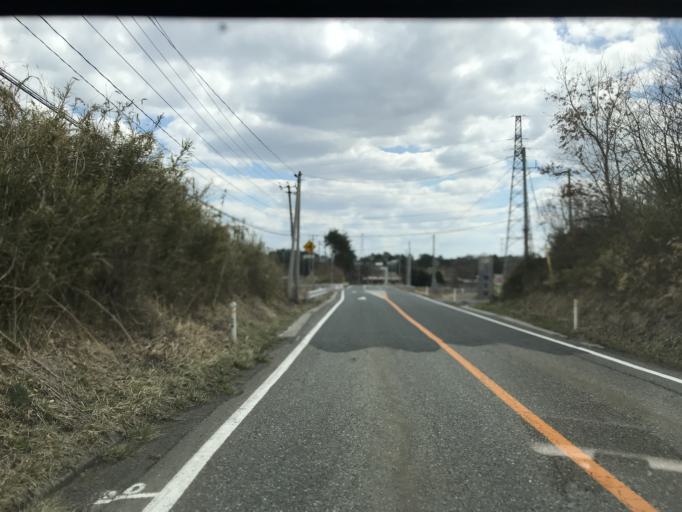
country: JP
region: Iwate
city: Ichinoseki
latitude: 38.8782
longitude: 141.1439
